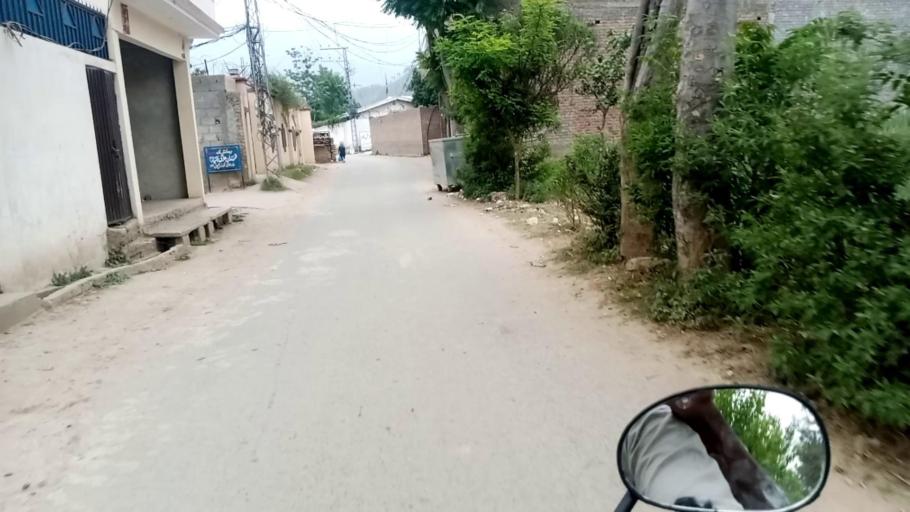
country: PK
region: Khyber Pakhtunkhwa
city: Saidu Sharif
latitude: 34.7554
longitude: 72.3828
